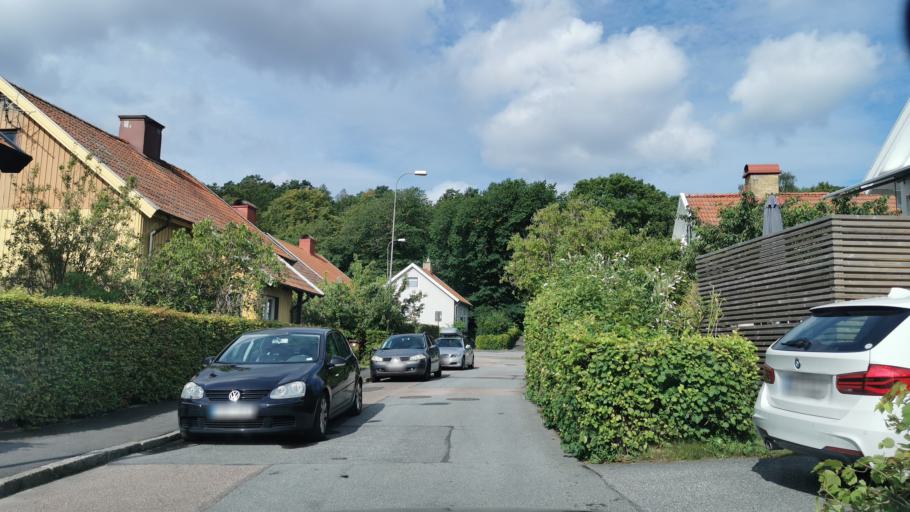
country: SE
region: Vaestra Goetaland
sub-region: Goteborg
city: Majorna
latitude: 57.6515
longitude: 11.9267
